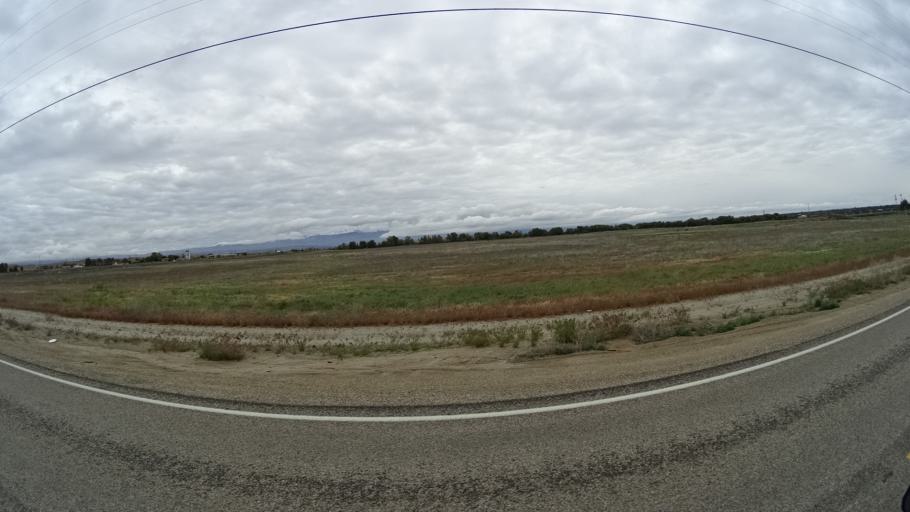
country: US
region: Idaho
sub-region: Ada County
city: Star
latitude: 43.7158
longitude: -116.4435
